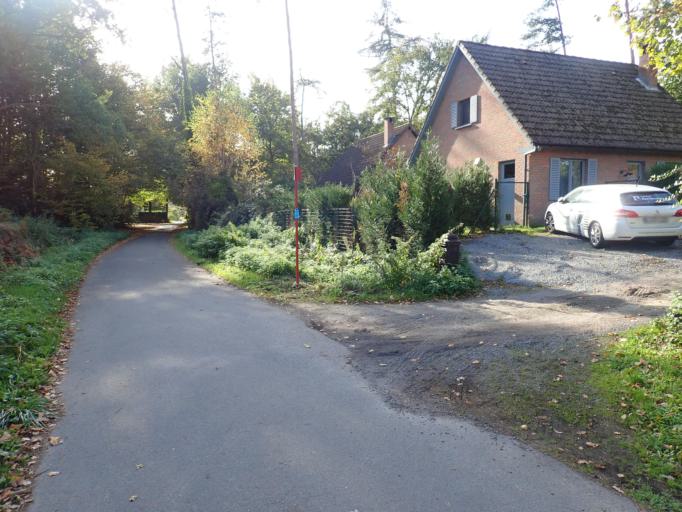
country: BE
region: Flanders
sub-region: Provincie Oost-Vlaanderen
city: Waasmunster
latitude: 51.1518
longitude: 4.0709
